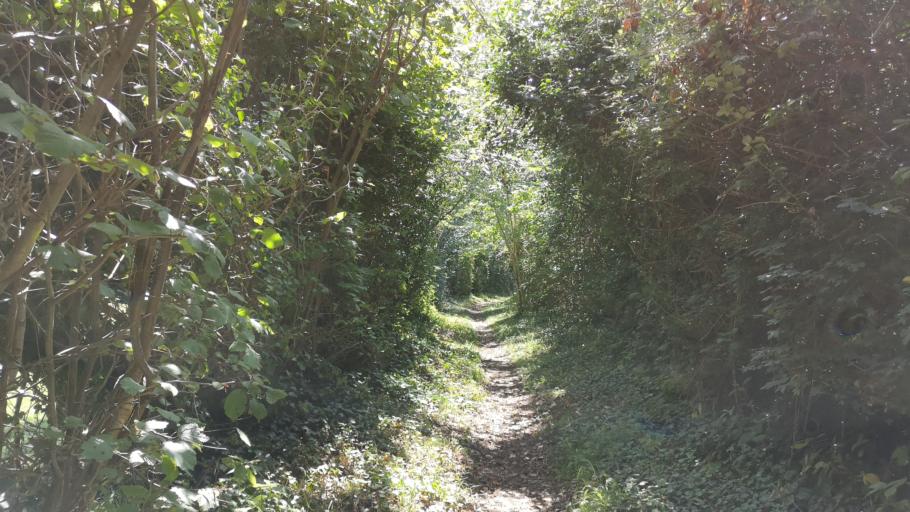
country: GB
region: England
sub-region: Isle of Wight
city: Brading
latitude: 50.6769
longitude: -1.1571
